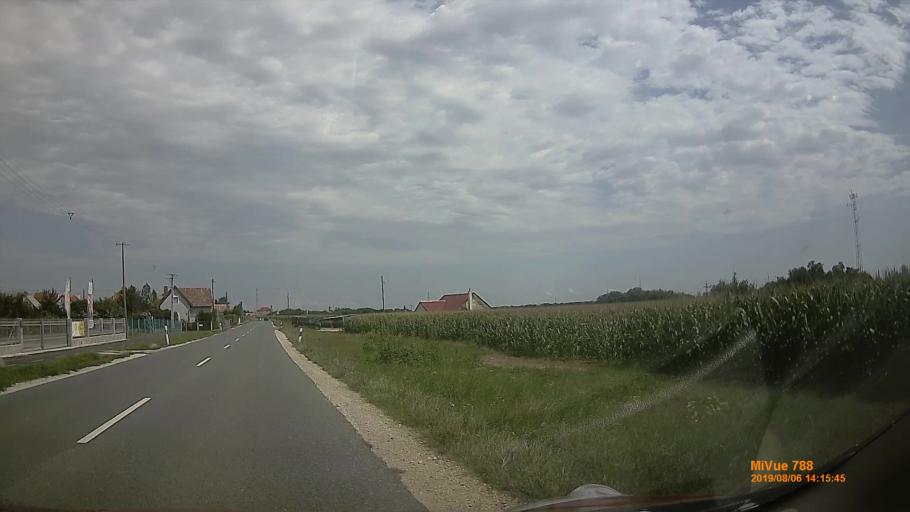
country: HU
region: Vas
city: Taplanszentkereszt
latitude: 47.1912
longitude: 16.7048
